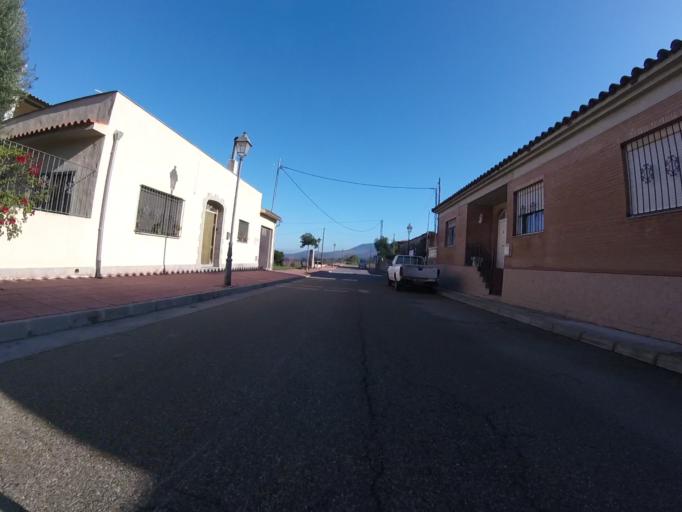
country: ES
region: Valencia
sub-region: Provincia de Castello
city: Santa Magdalena de Pulpis
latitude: 40.3562
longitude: 0.3052
